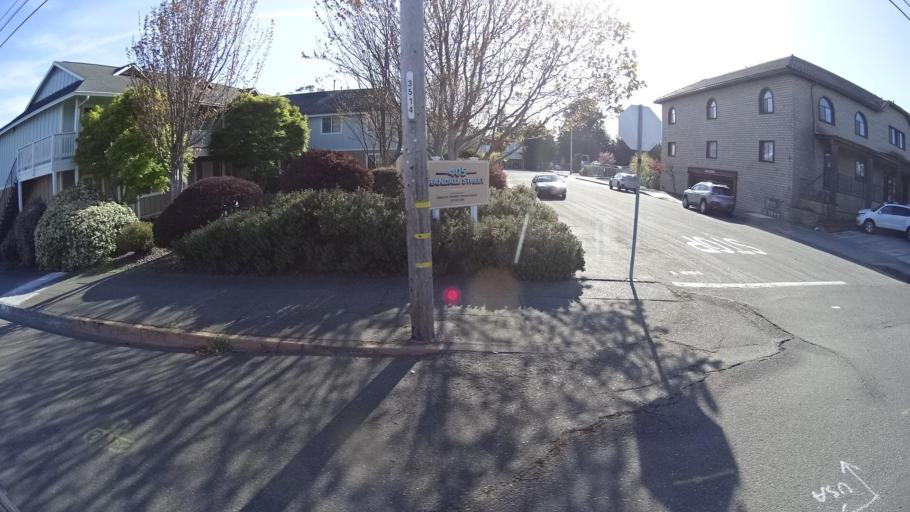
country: US
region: California
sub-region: Humboldt County
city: Eureka
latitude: 40.7920
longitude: -124.1647
